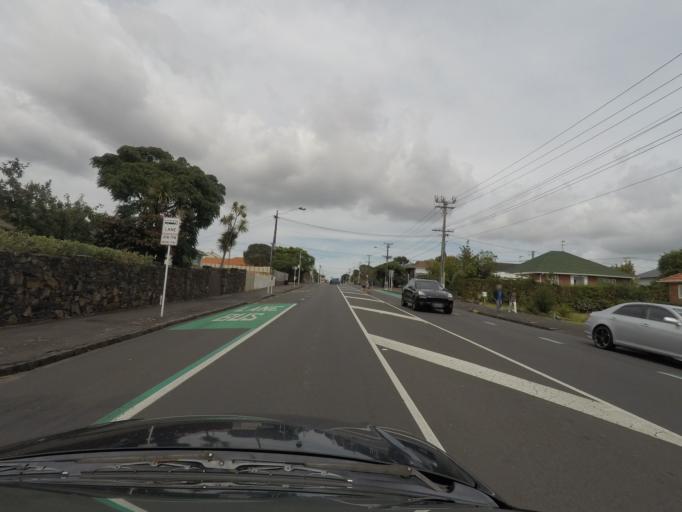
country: NZ
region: Auckland
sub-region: Auckland
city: Auckland
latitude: -36.8822
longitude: 174.7394
